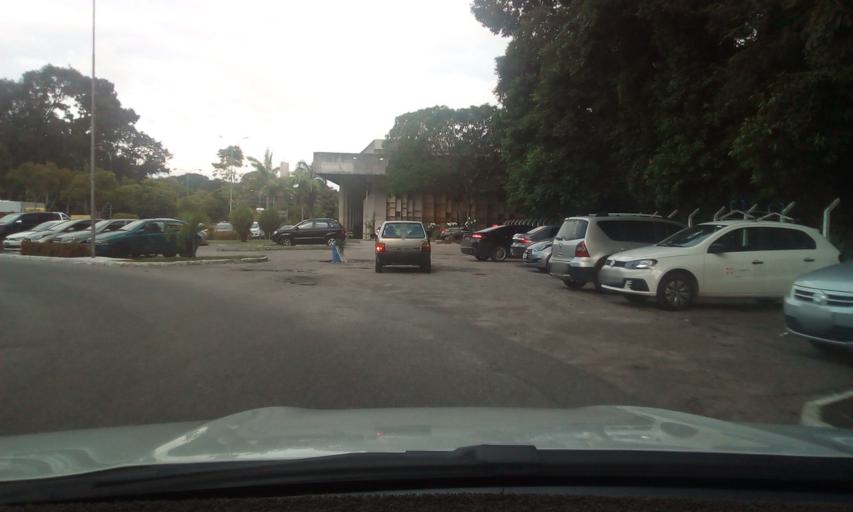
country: BR
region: Paraiba
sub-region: Joao Pessoa
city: Joao Pessoa
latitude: -7.1381
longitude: -34.8478
